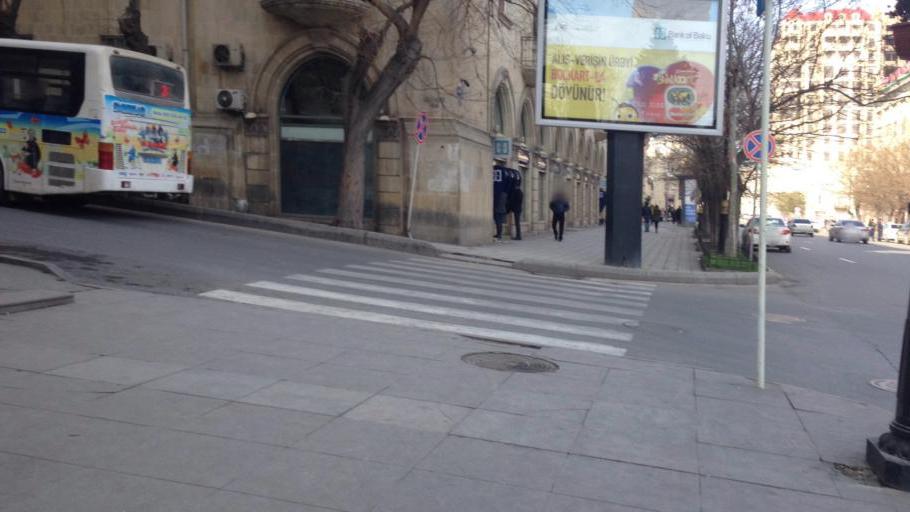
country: AZ
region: Baki
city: Badamdar
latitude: 40.3694
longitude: 49.8347
